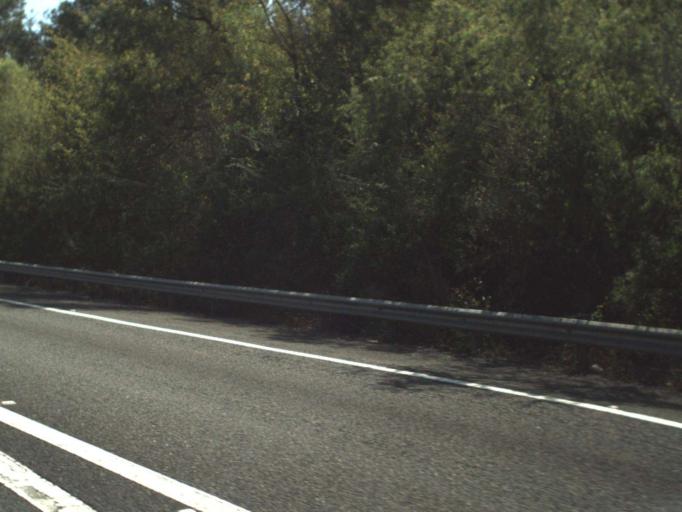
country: US
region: Florida
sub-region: Escambia County
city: Cantonment
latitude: 30.5676
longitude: -87.3932
